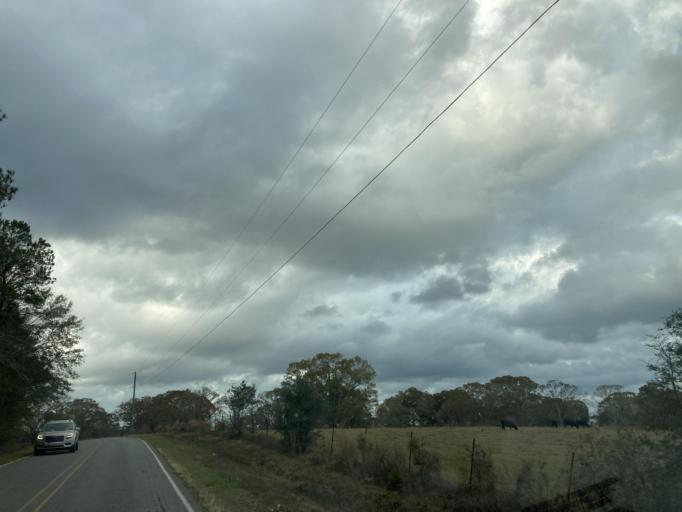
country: US
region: Mississippi
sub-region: Marion County
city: Columbia
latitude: 31.1864
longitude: -89.6643
